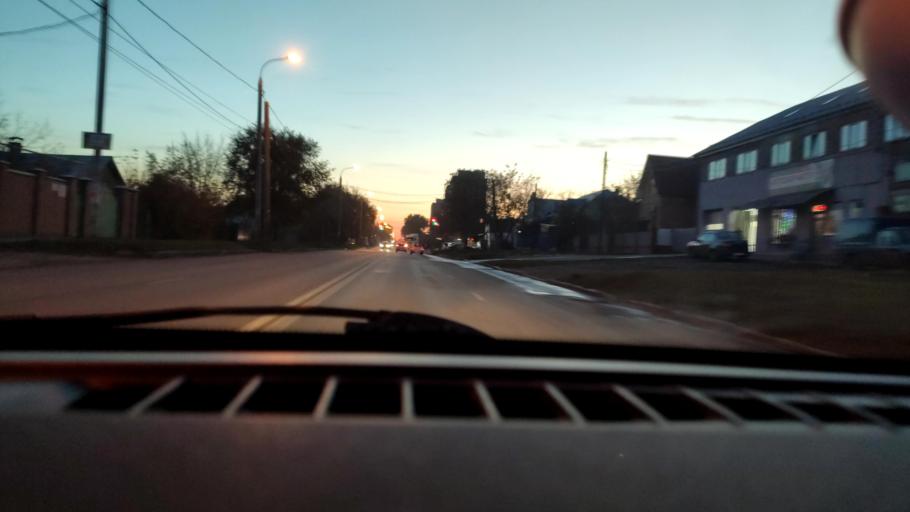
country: RU
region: Samara
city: Samara
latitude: 53.1890
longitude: 50.2086
